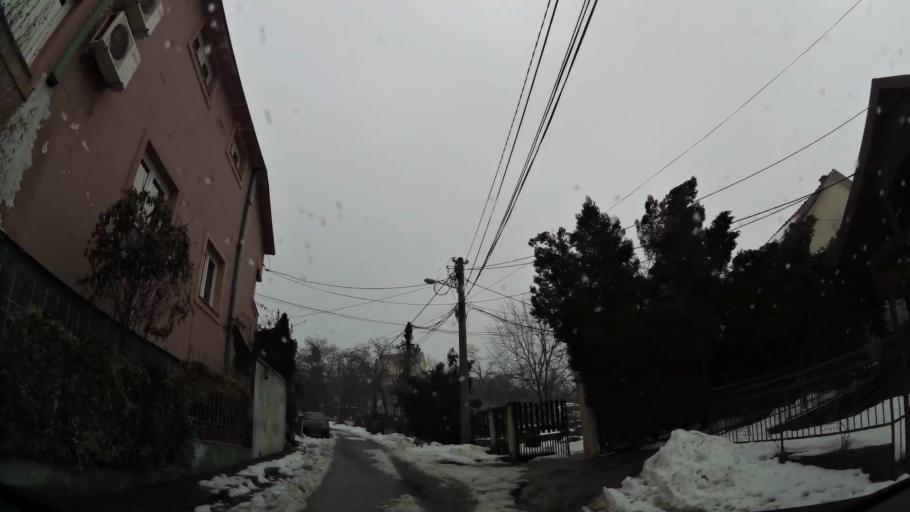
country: RS
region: Central Serbia
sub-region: Belgrade
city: Zvezdara
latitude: 44.7730
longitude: 20.5270
